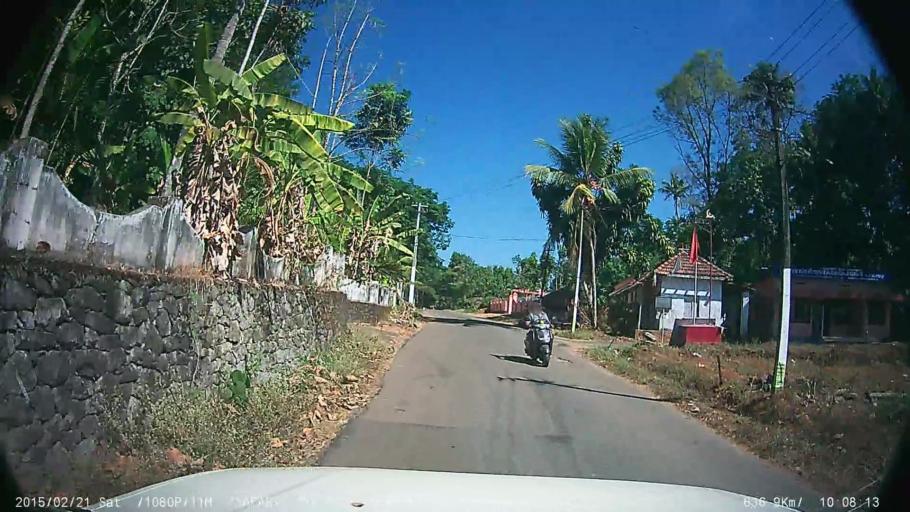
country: IN
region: Kerala
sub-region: Ernakulam
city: Piravam
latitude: 9.8777
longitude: 76.6064
